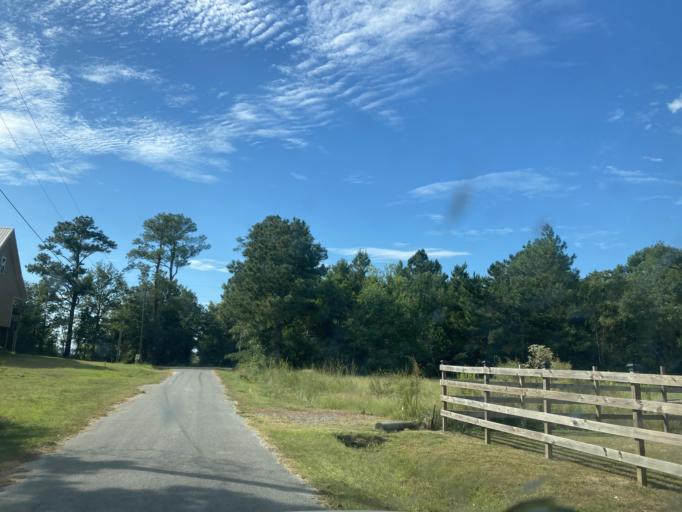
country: US
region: Mississippi
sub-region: Jackson County
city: Saint Martin
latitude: 30.4319
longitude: -88.8612
